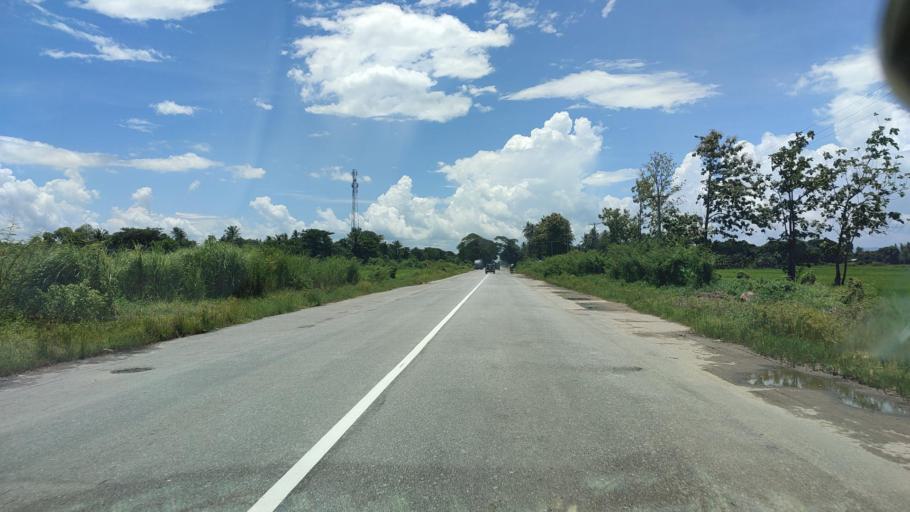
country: MM
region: Bago
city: Taungoo
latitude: 18.7264
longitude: 96.4076
